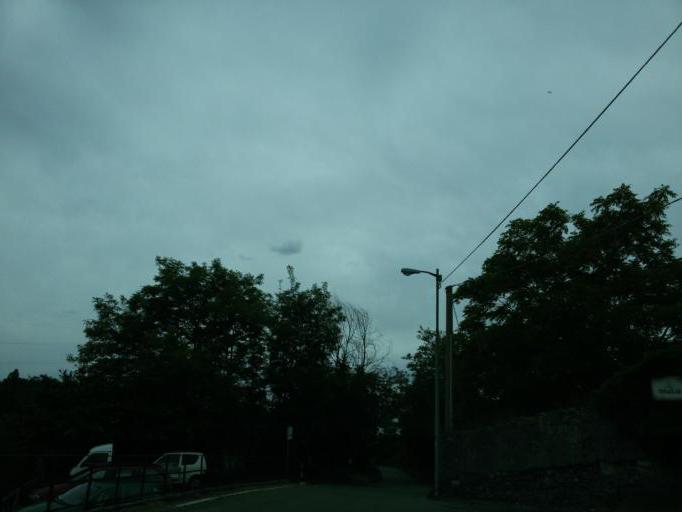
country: IT
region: Liguria
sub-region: Provincia di Genova
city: San Teodoro
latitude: 44.4228
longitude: 8.9038
